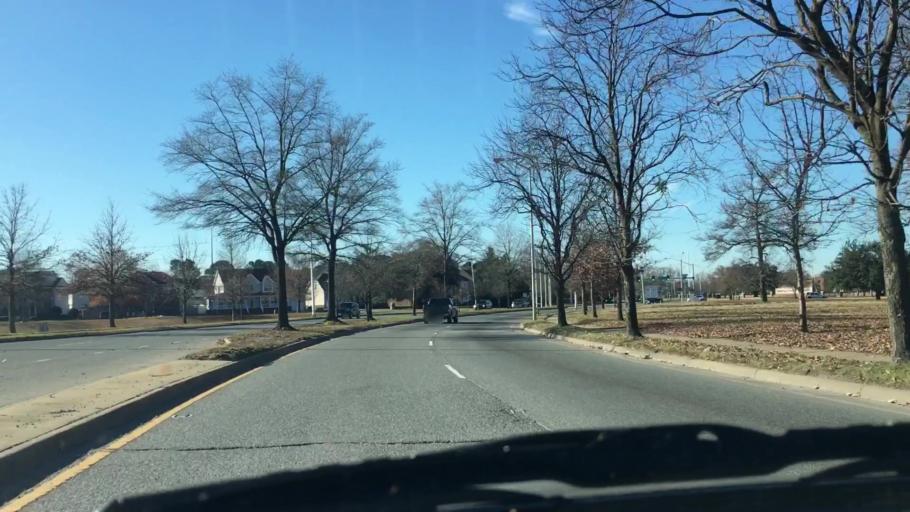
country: US
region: Virginia
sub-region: City of Norfolk
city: Norfolk
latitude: 36.8492
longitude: -76.2492
